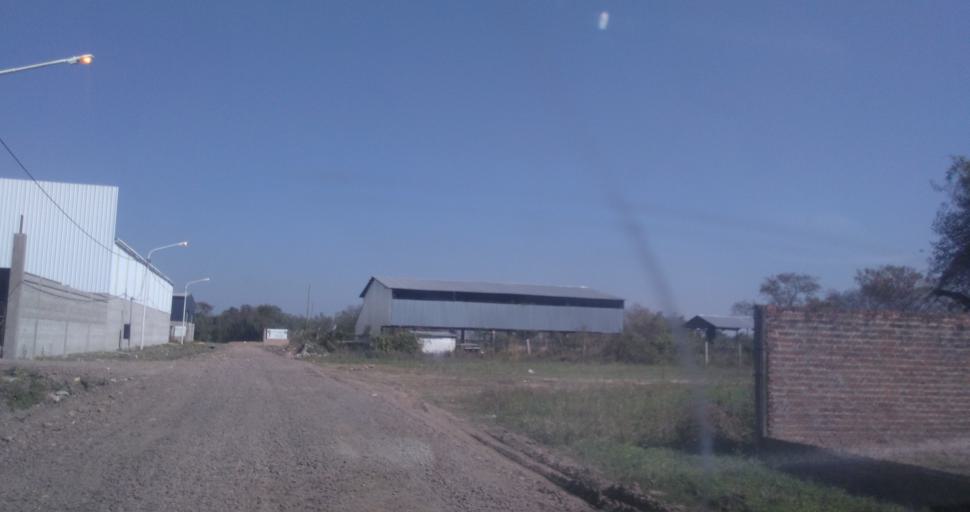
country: AR
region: Chaco
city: Fontana
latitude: -27.4346
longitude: -59.0300
